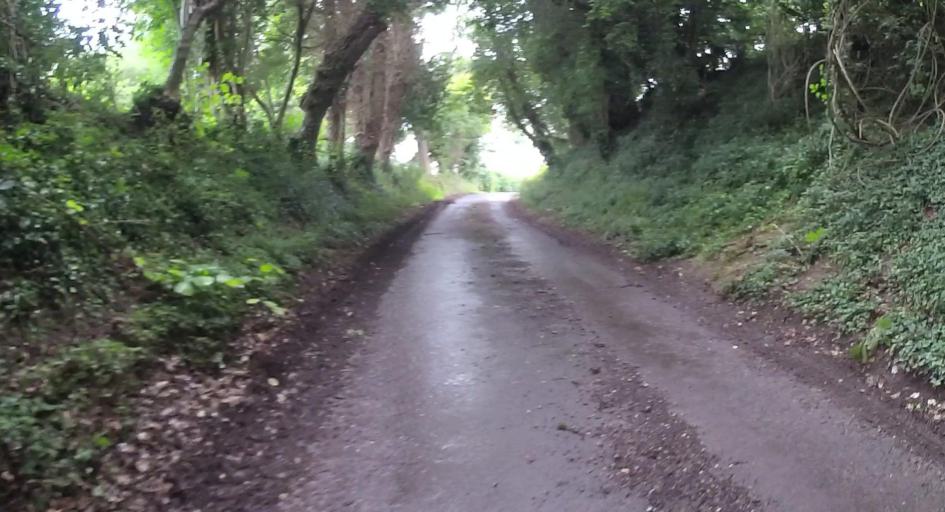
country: GB
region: England
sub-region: Hampshire
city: Highclere
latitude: 51.2557
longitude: -1.4123
